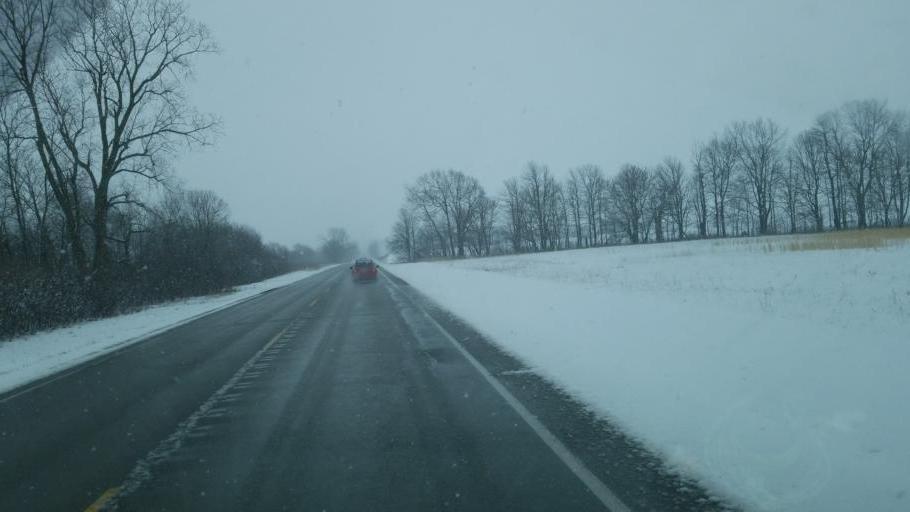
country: US
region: Indiana
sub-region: Randolph County
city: Parker City
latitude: 40.0456
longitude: -85.2165
